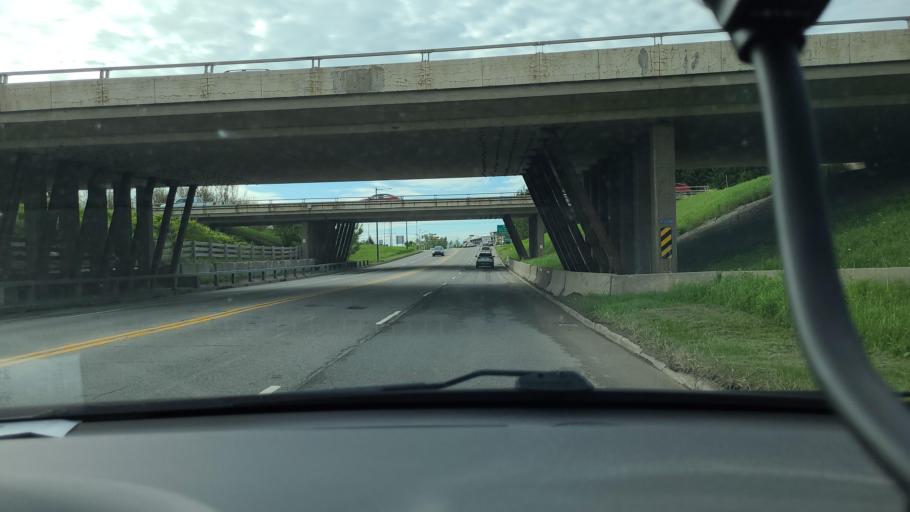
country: CA
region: Quebec
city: L'Ancienne-Lorette
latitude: 46.7666
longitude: -71.3730
